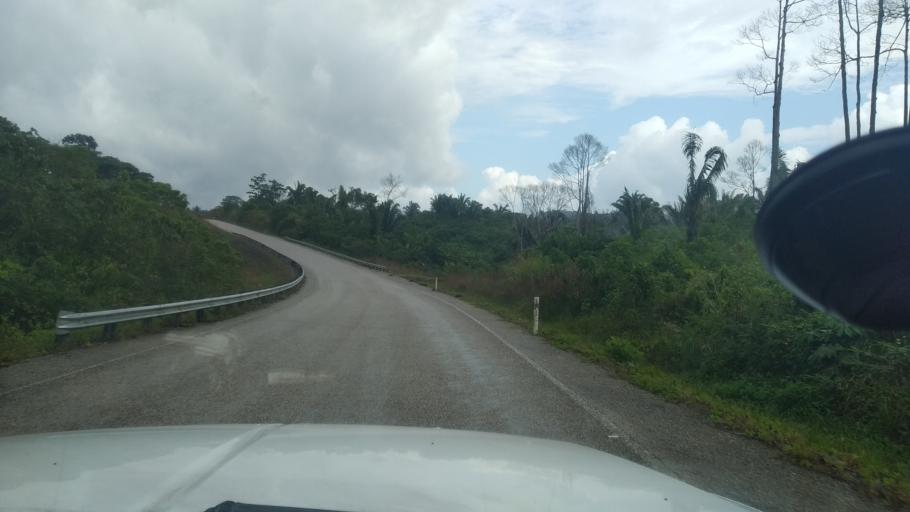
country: GT
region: Peten
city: San Luis
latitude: 16.1958
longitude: -89.1639
